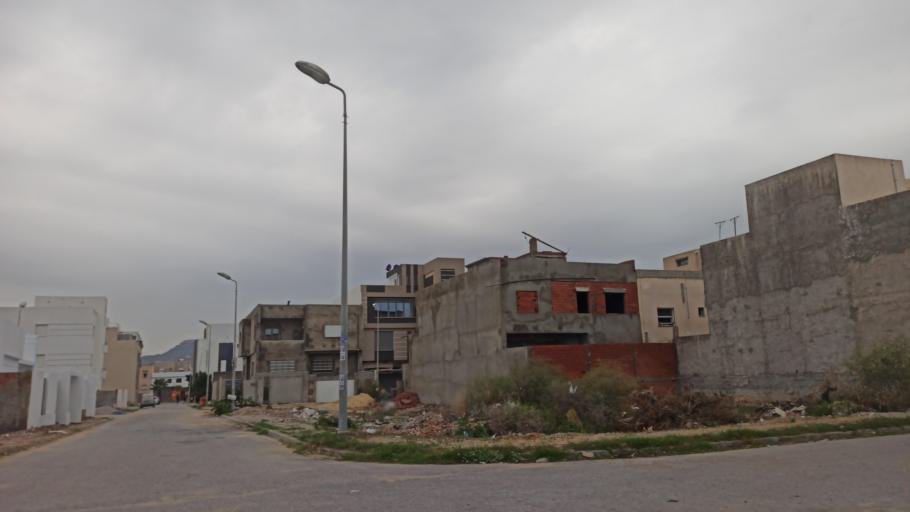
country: TN
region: Tunis
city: Hammam-Lif
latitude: 36.7103
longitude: 10.4143
